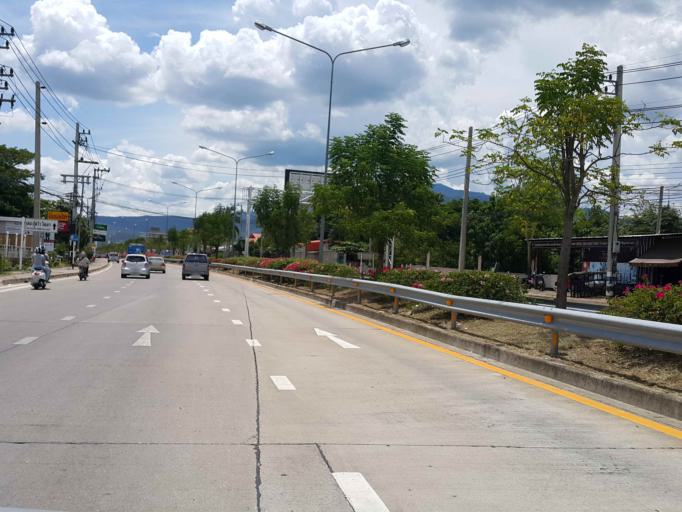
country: TH
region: Chiang Mai
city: Chiang Mai
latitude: 18.7448
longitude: 98.9567
